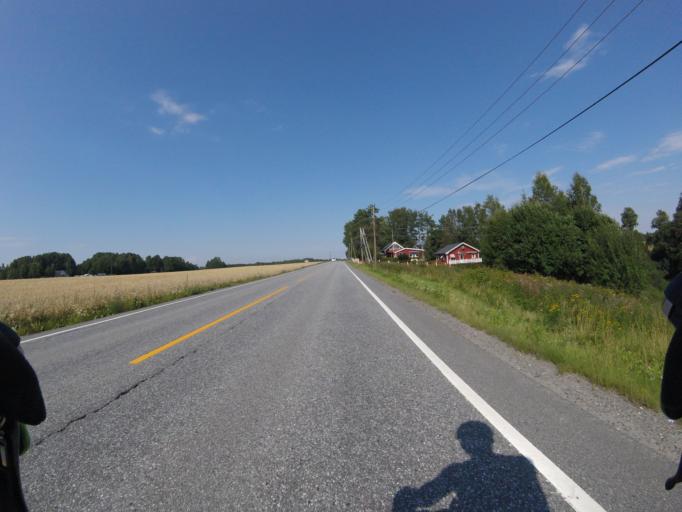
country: NO
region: Akershus
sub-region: Ullensaker
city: Klofta
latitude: 60.0554
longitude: 11.1181
